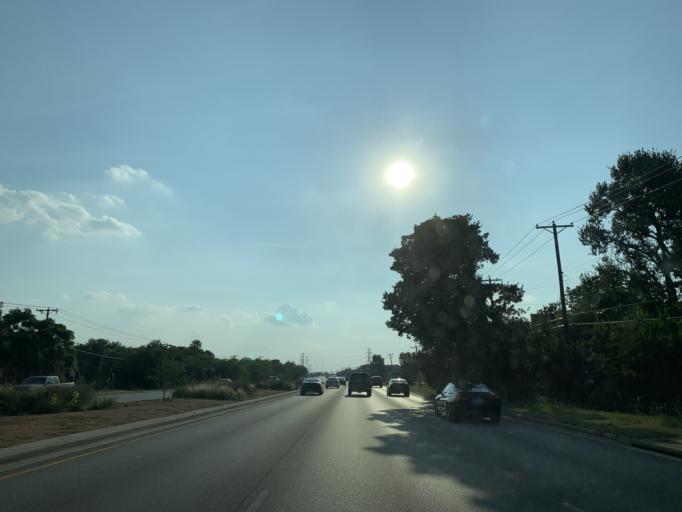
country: US
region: Texas
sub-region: Tarrant County
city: Hurst
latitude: 32.8093
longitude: -97.1913
